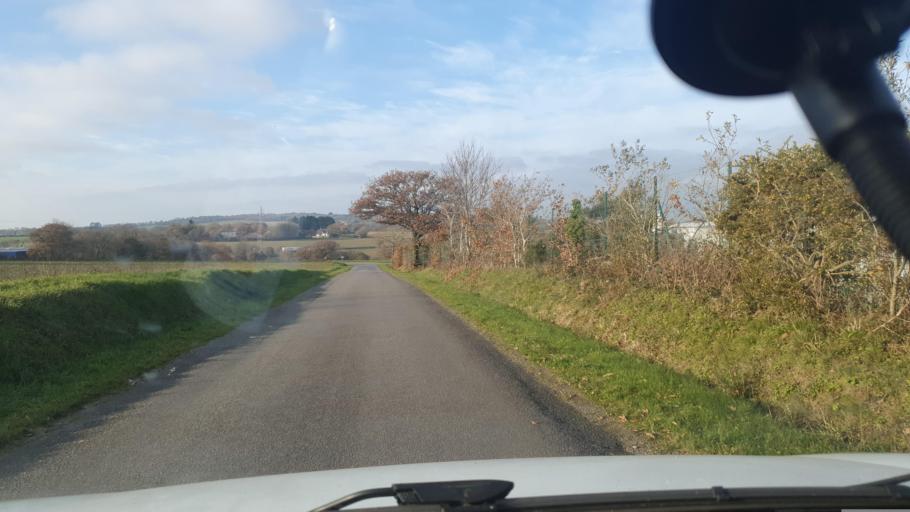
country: FR
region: Brittany
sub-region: Departement du Finistere
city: Briec
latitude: 48.1062
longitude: -4.0215
